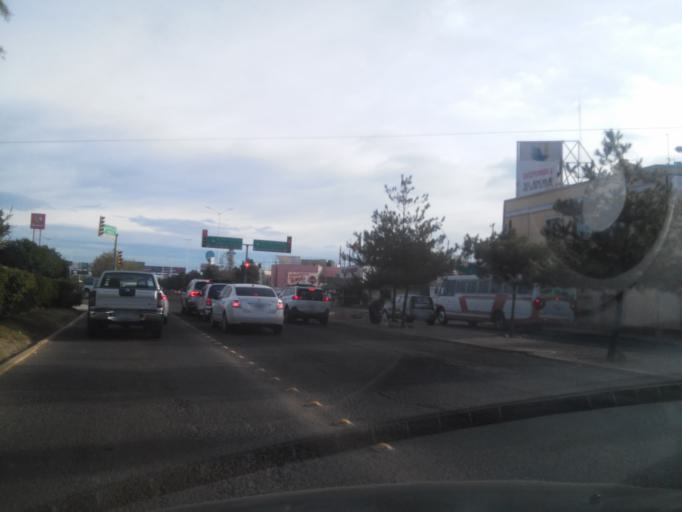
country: MX
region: Durango
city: Victoria de Durango
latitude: 24.0398
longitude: -104.6315
